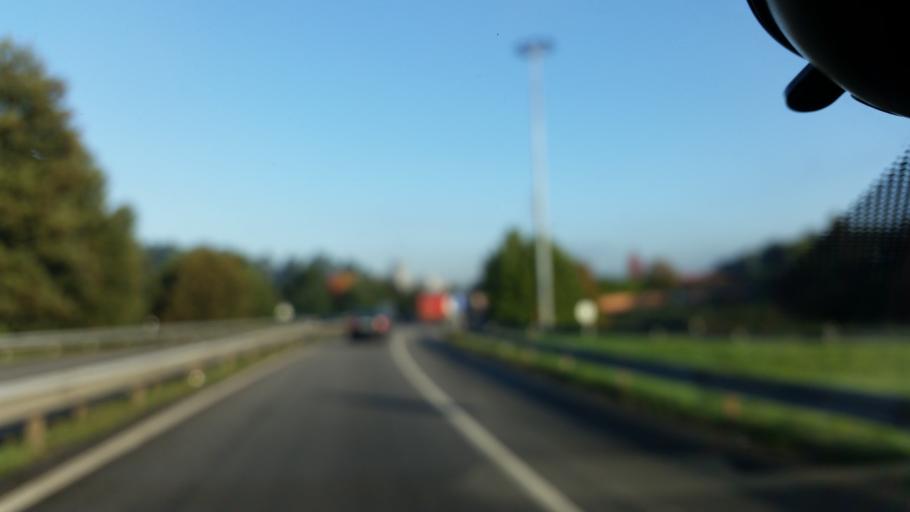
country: PT
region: Porto
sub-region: Santo Tirso
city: Sao Miguel do Couto
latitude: 41.3279
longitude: -8.4708
